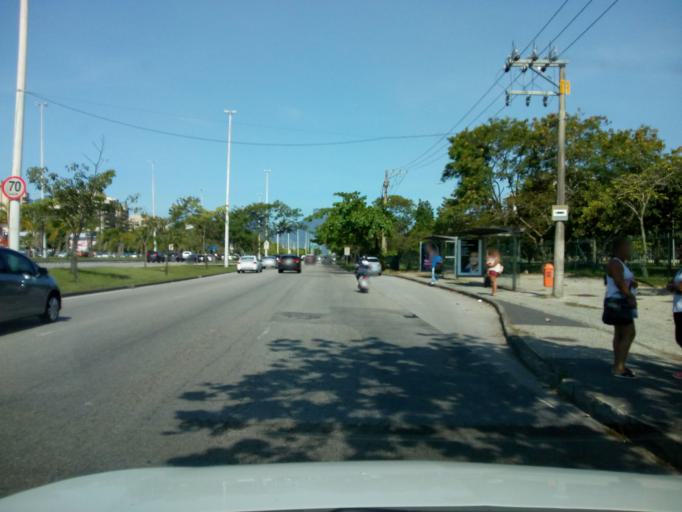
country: BR
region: Rio de Janeiro
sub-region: Nilopolis
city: Nilopolis
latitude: -23.0007
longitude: -43.3816
